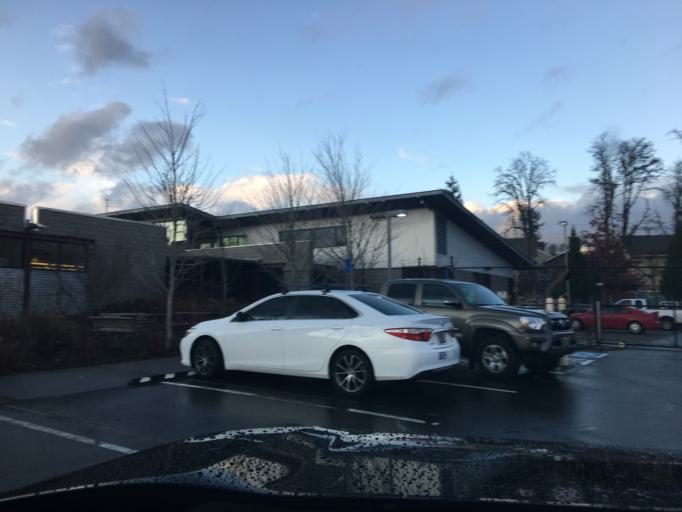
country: US
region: Oregon
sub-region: Washington County
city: Aloha
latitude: 45.5039
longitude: -122.8459
